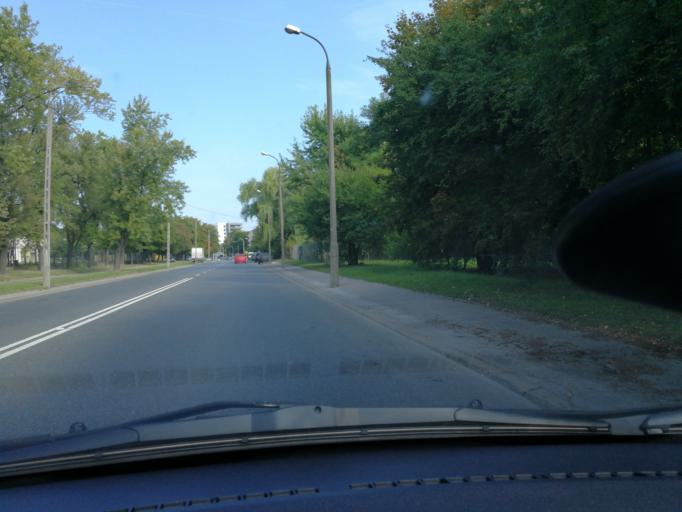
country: PL
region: Masovian Voivodeship
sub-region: Warszawa
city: Bemowo
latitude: 52.2310
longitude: 20.9420
